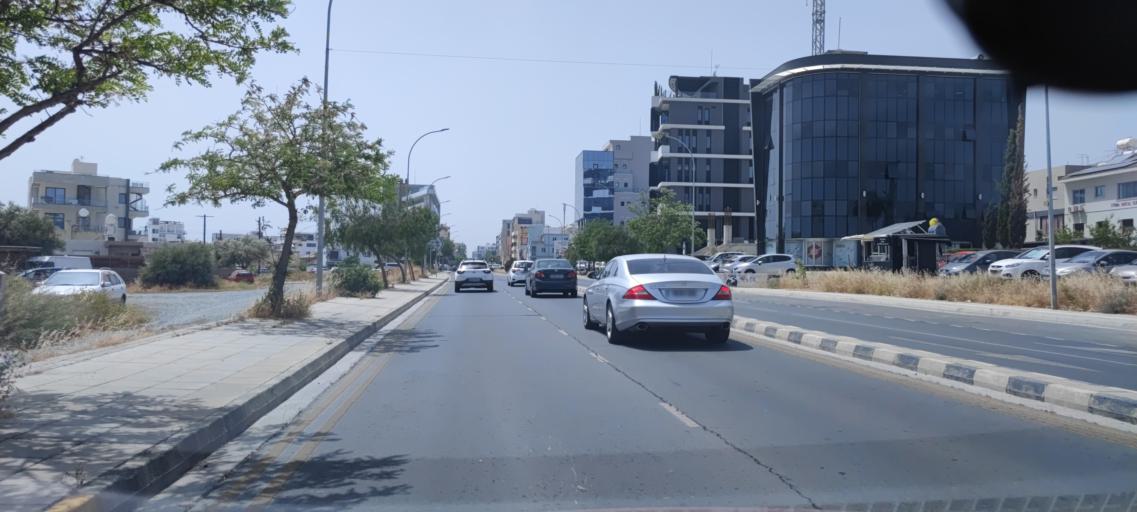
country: CY
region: Limassol
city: Limassol
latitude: 34.6986
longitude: 33.0539
